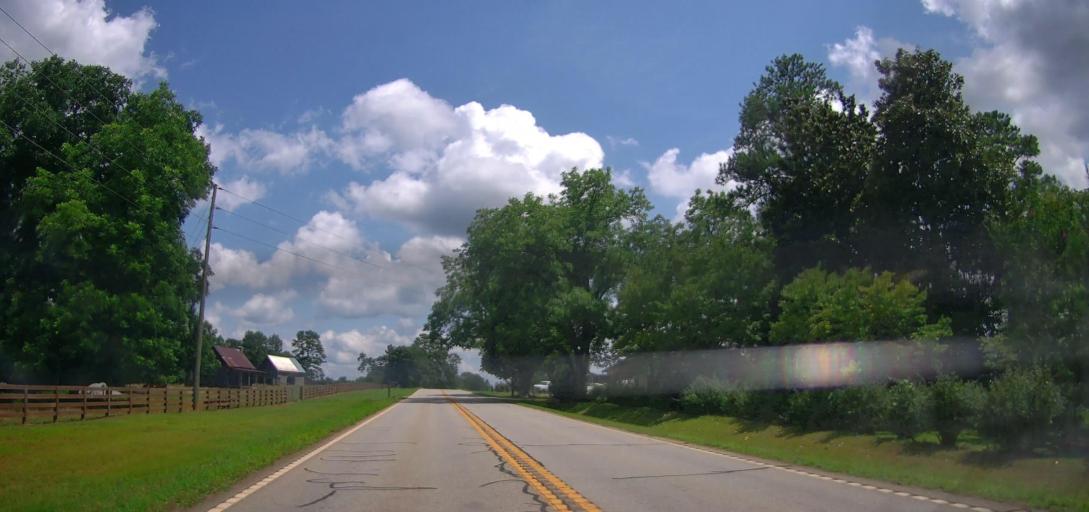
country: US
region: Georgia
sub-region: Heard County
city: Franklin
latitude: 33.3421
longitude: -85.1685
